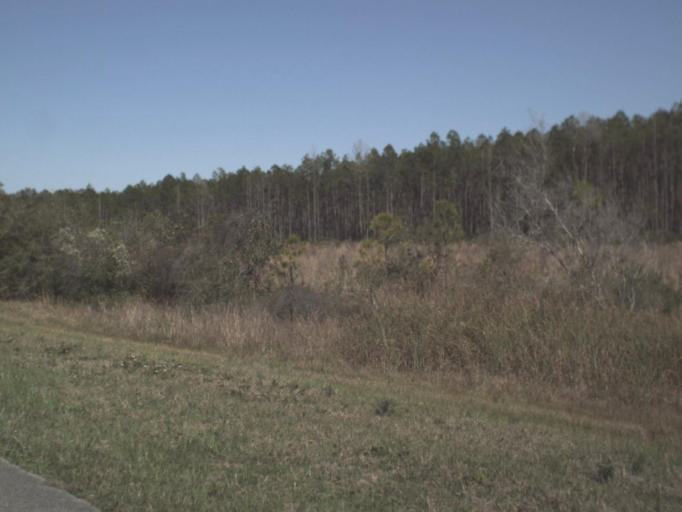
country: US
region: Florida
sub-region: Gulf County
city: Port Saint Joe
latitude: 29.9147
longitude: -85.2025
